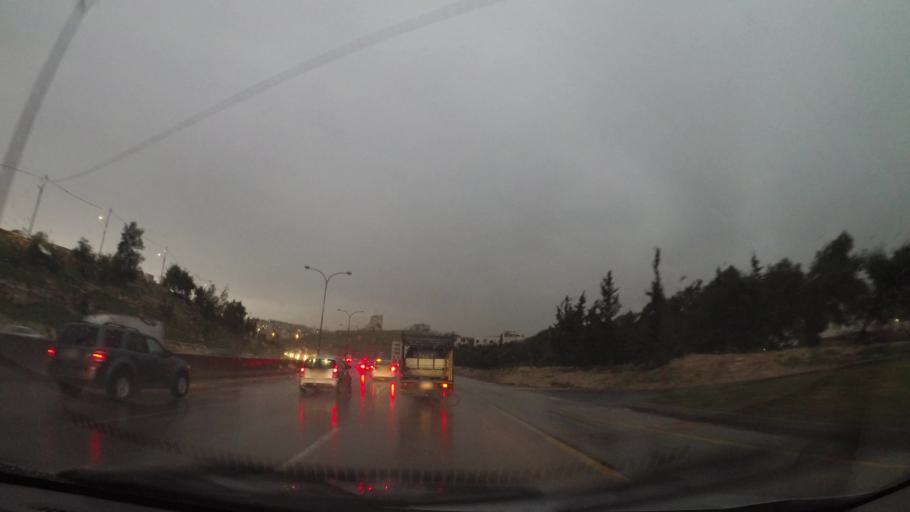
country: JO
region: Amman
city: Umm as Summaq
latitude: 31.9054
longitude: 35.8689
